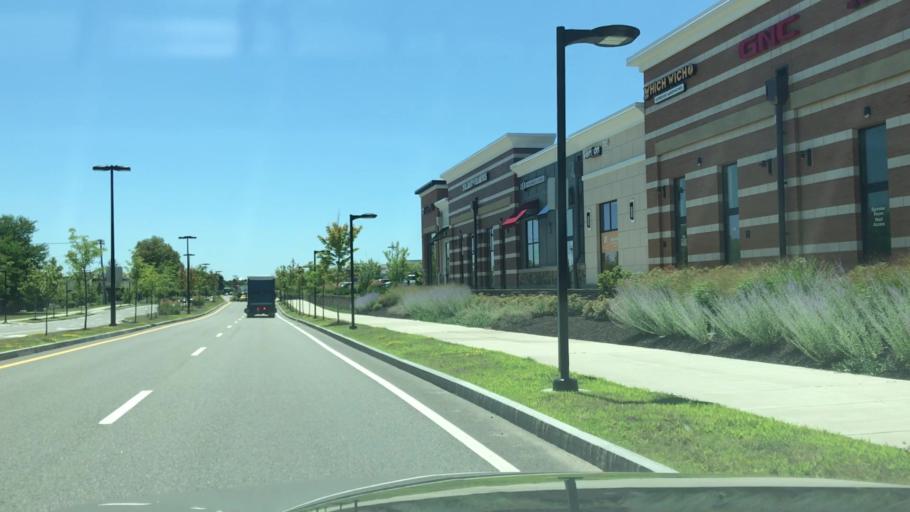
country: US
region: Massachusetts
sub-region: Norfolk County
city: Dedham
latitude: 42.2073
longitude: -71.1519
